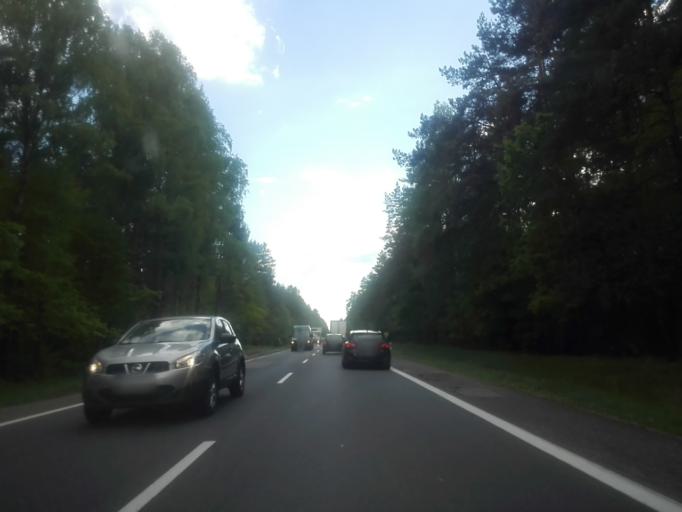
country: PL
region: Masovian Voivodeship
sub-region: Powiat wyszkowski
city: Dlugosiodlo
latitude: 52.7004
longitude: 21.6666
